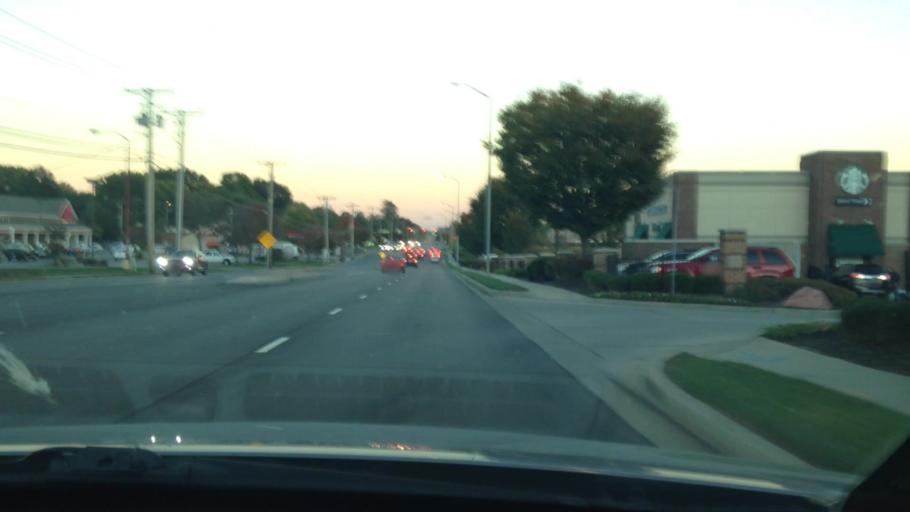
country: US
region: Kansas
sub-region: Johnson County
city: Overland Park
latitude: 38.9566
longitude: -94.6895
